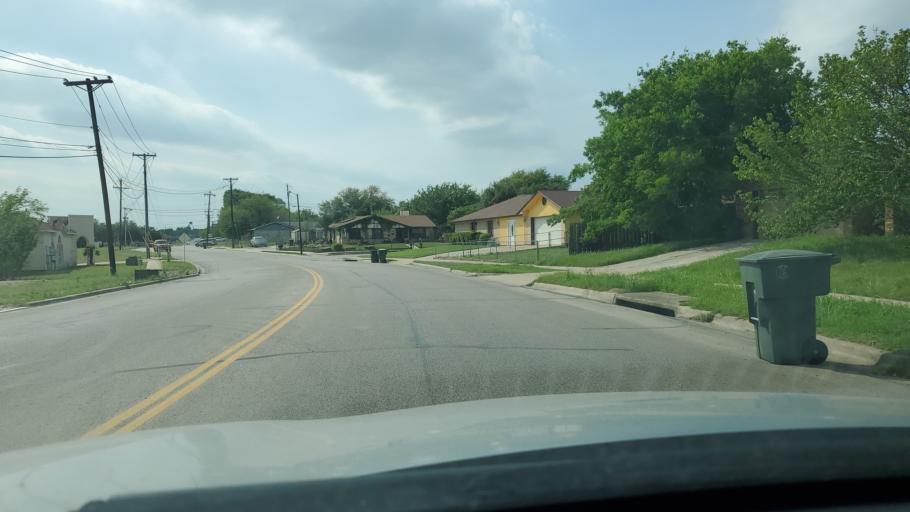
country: US
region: Texas
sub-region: Bell County
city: Killeen
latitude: 31.0932
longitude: -97.7114
